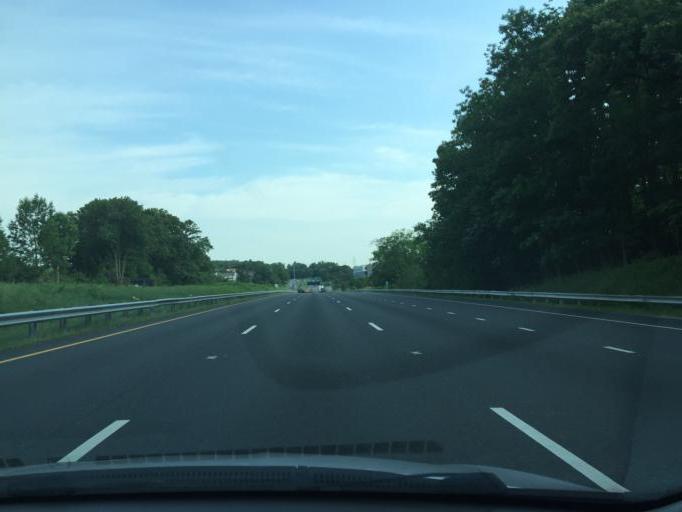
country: US
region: Maryland
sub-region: Baltimore County
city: Lutherville
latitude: 39.3801
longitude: -76.6605
